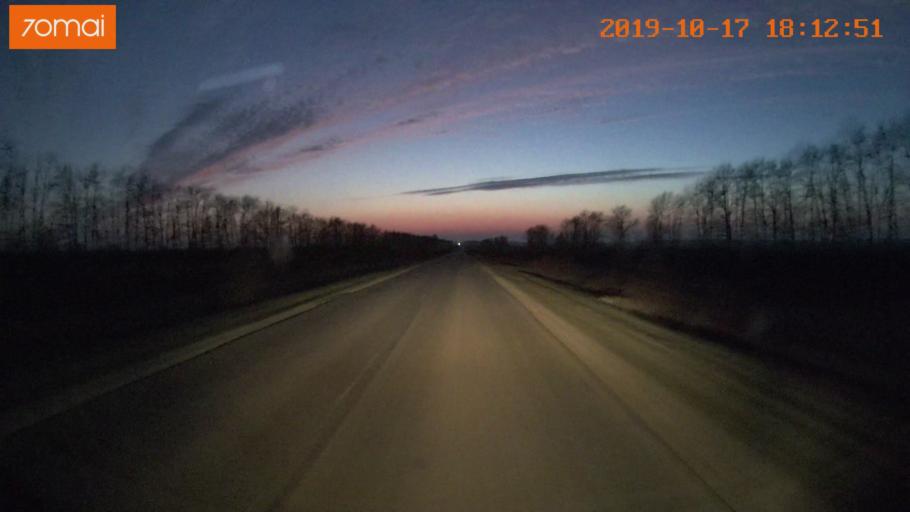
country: RU
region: Tula
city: Kurkino
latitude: 53.4114
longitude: 38.6023
